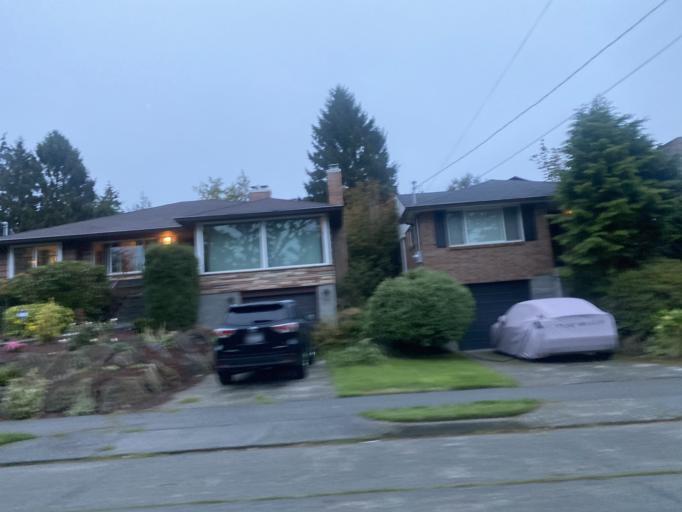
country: US
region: Washington
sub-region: King County
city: Seattle
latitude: 47.6455
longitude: -122.3983
